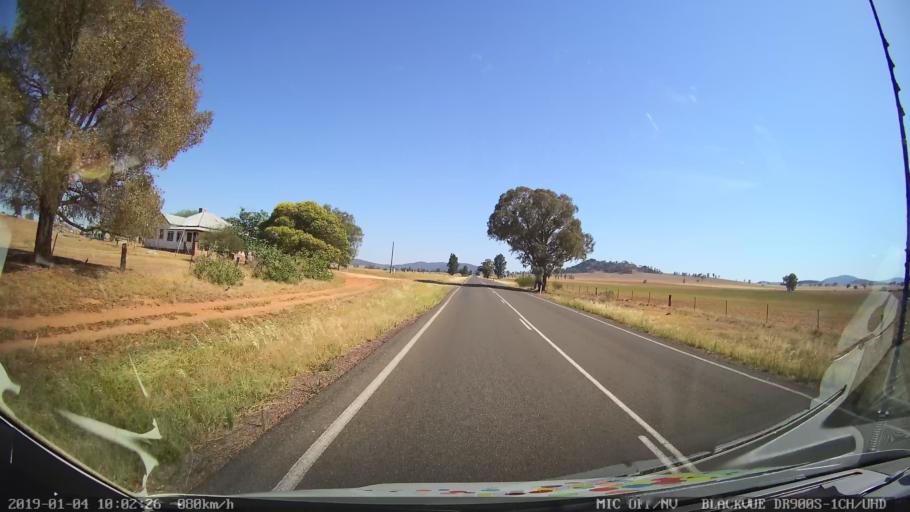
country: AU
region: New South Wales
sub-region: Cabonne
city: Canowindra
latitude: -33.4763
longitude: 148.3654
